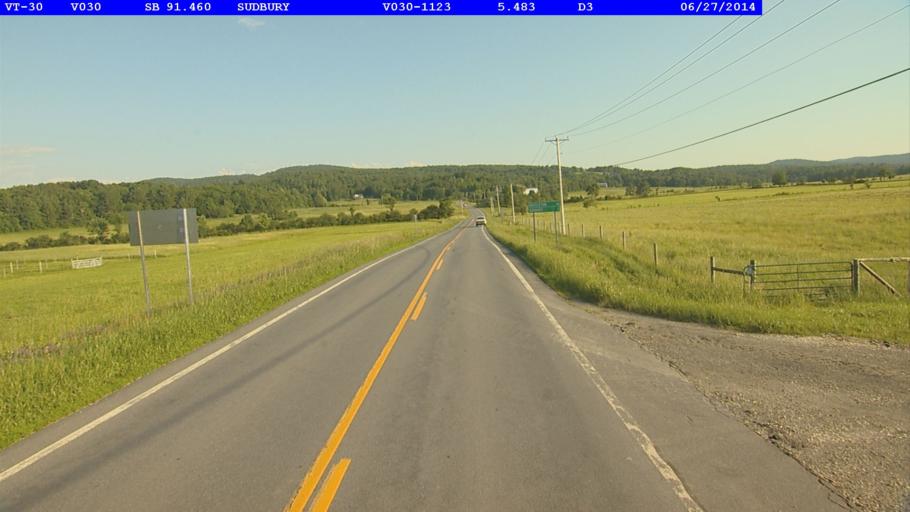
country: US
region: Vermont
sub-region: Rutland County
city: Brandon
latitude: 43.8251
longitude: -73.1934
